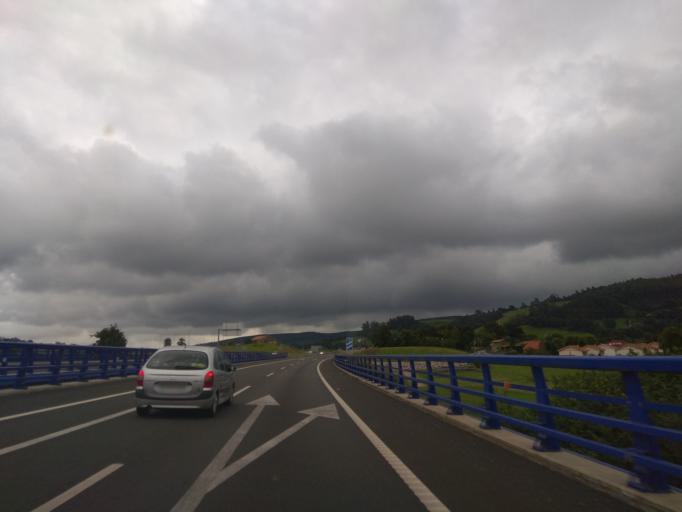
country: ES
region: Cantabria
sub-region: Provincia de Cantabria
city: Penagos
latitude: 43.3358
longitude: -3.8233
